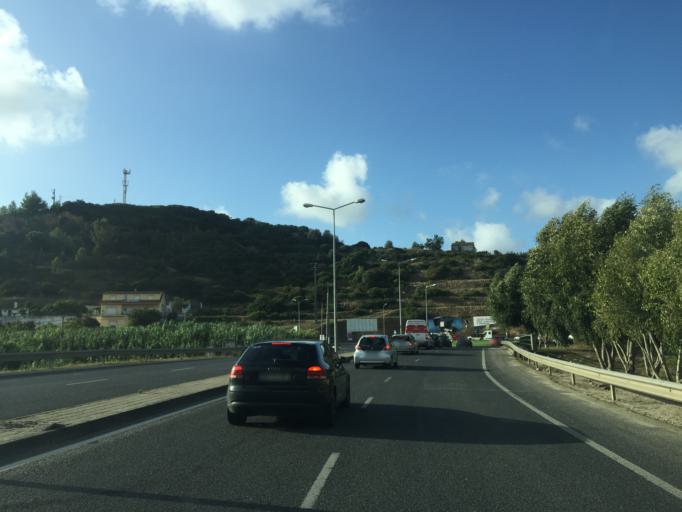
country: PT
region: Lisbon
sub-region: Torres Vedras
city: Torres Vedras
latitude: 39.0950
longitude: -9.2684
